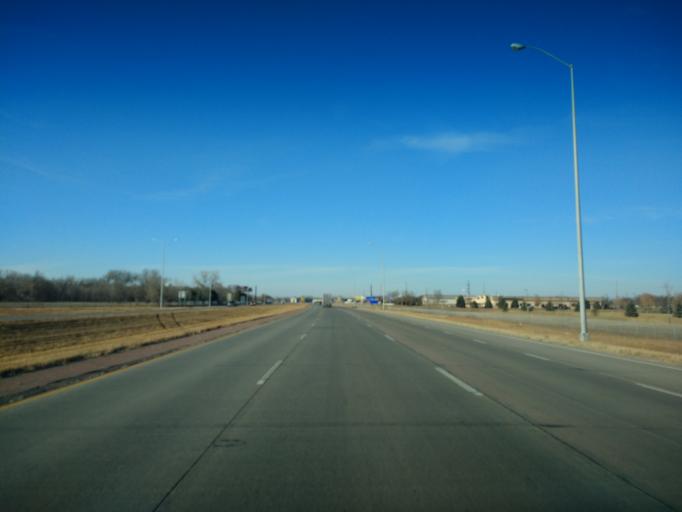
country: US
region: South Dakota
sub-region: Union County
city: Dakota Dunes
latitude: 42.5078
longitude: -96.4919
